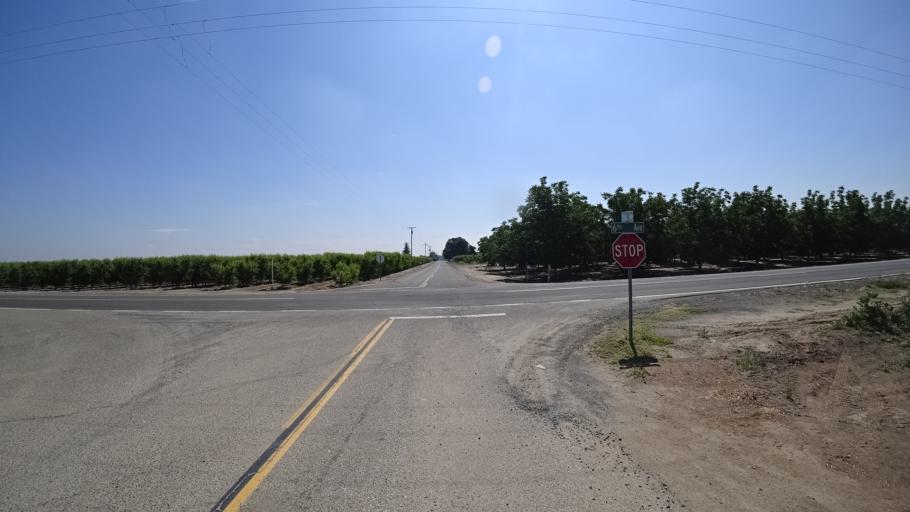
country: US
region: California
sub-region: Fresno County
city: Kingsburg
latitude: 36.4596
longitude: -119.5647
